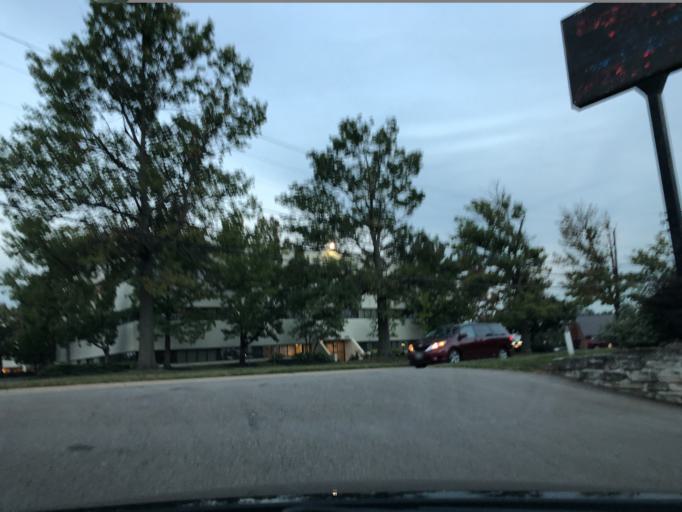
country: US
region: Ohio
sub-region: Hamilton County
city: Sixteen Mile Stand
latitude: 39.2608
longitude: -84.3412
